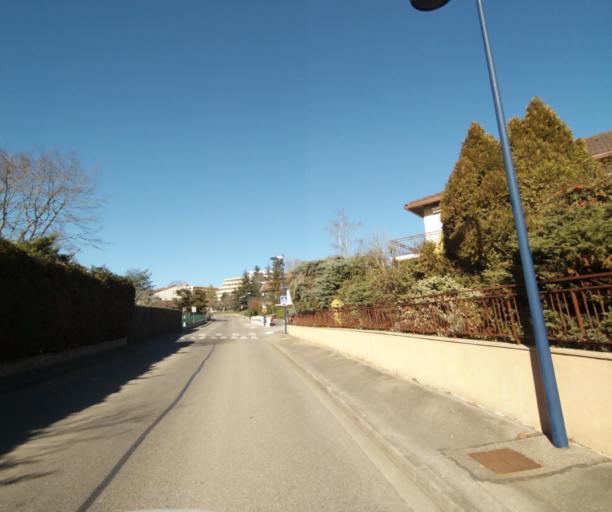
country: FR
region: Lorraine
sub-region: Departement de Meurthe-et-Moselle
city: Ludres
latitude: 48.6137
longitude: 6.1687
